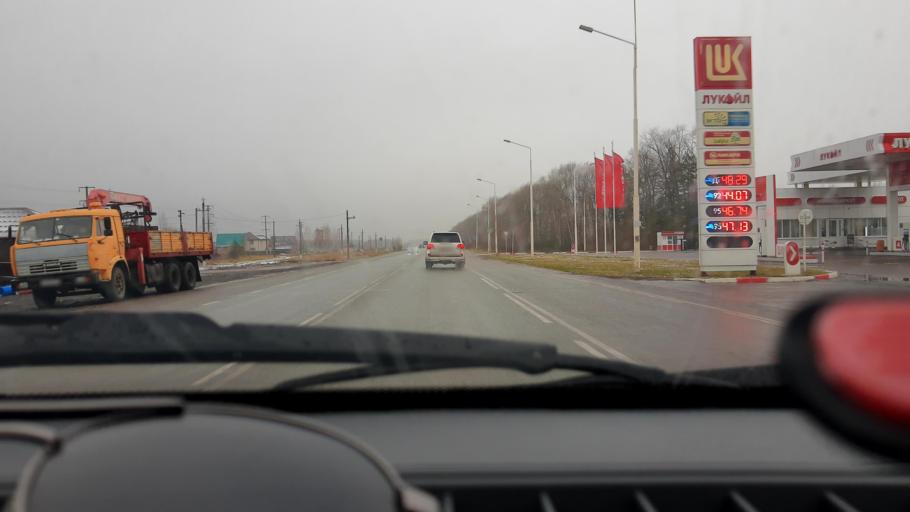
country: RU
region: Bashkortostan
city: Kabakovo
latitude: 54.6069
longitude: 56.1841
